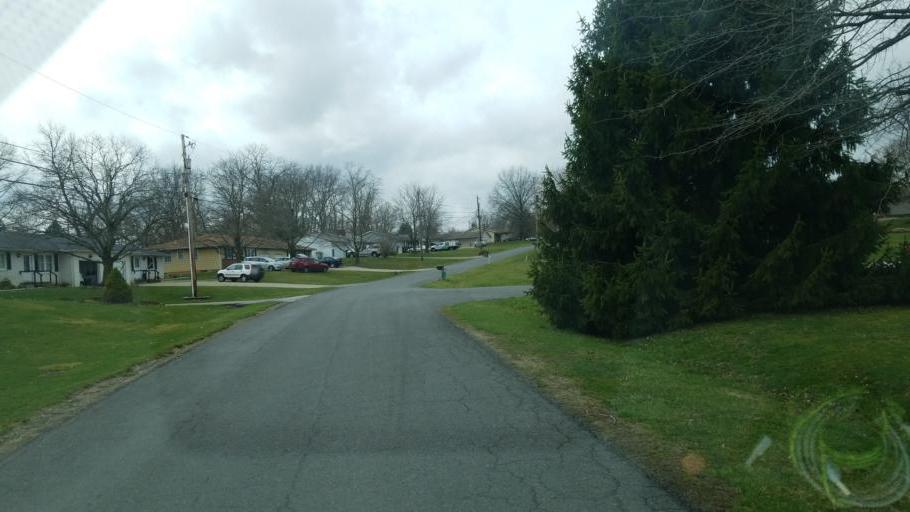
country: US
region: Ohio
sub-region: Wayne County
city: Wooster
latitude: 40.7666
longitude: -81.9600
